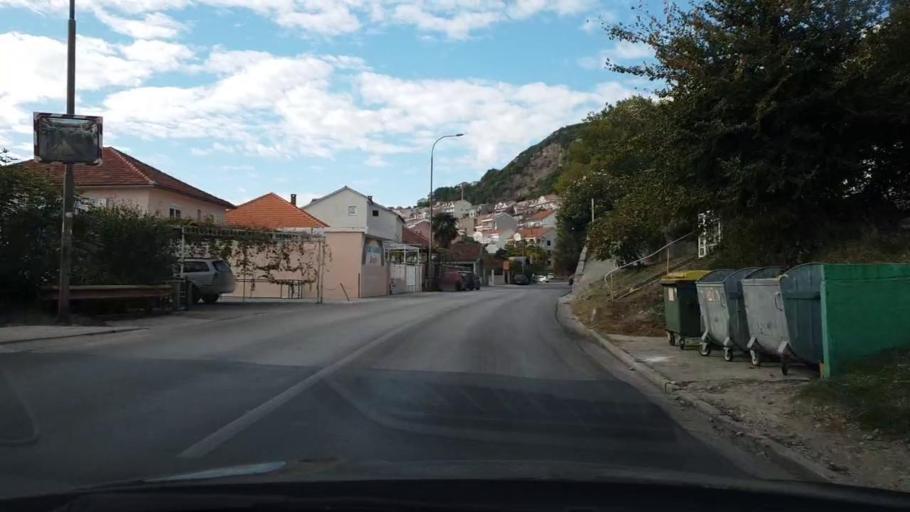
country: ME
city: Igalo
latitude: 42.4611
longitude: 18.5150
